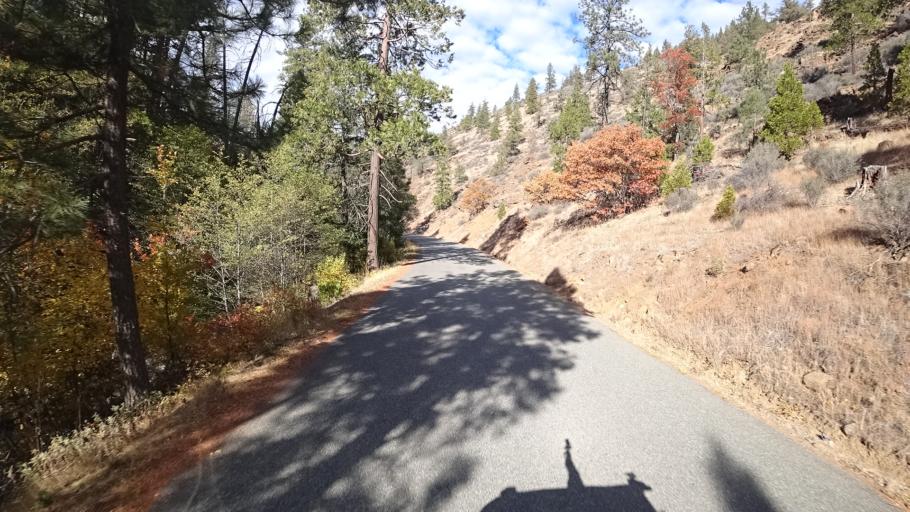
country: US
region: California
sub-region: Siskiyou County
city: Yreka
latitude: 41.6319
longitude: -122.7314
